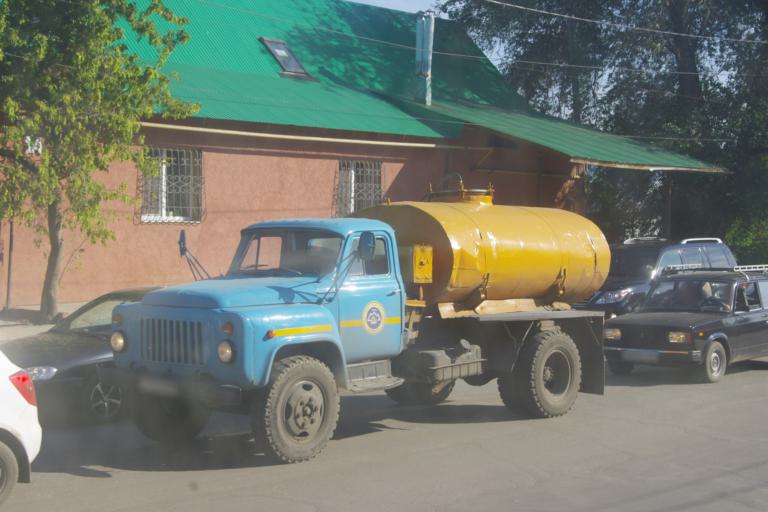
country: RU
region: Samara
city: Samara
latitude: 53.1945
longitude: 50.2170
